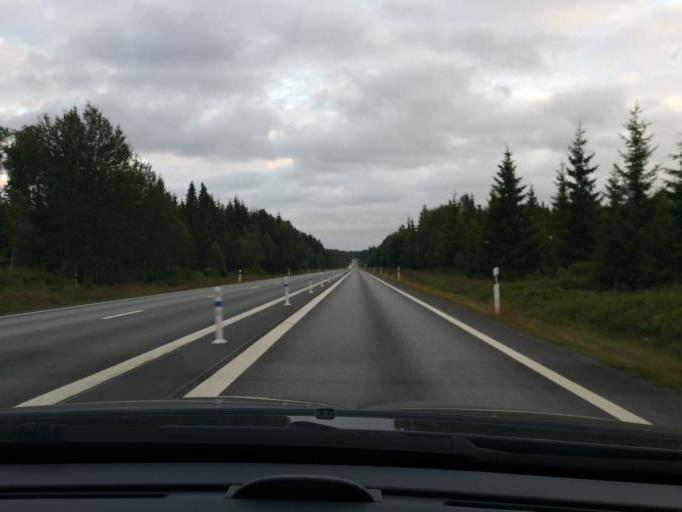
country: SE
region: Kronoberg
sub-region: Vaxjo Kommun
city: Lammhult
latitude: 57.1088
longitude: 14.6357
